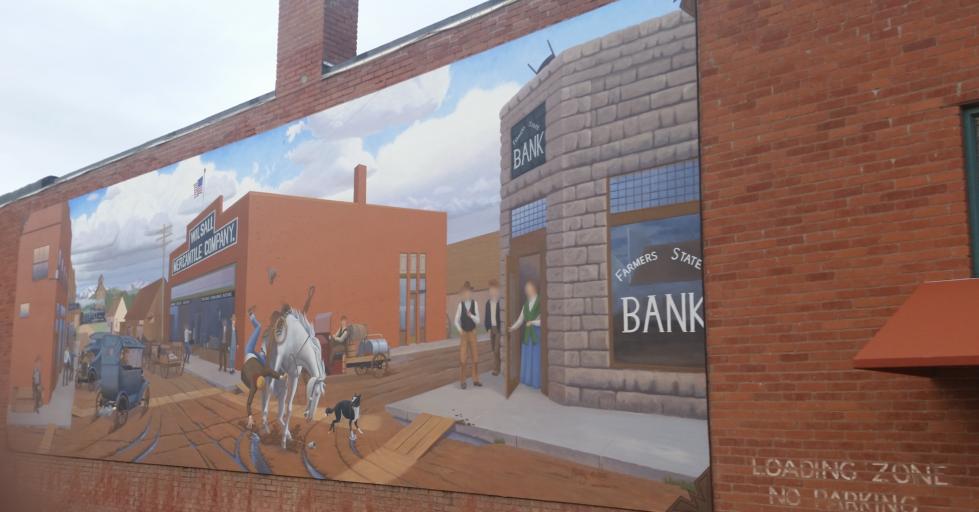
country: US
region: Montana
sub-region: Park County
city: Livingston
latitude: 45.9934
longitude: -110.6603
